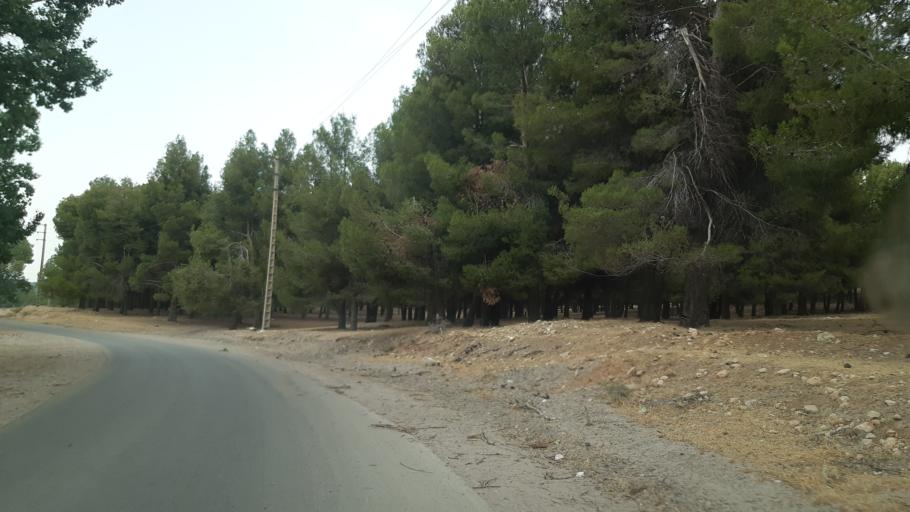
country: MA
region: Meknes-Tafilalet
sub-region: Ifrane
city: Ifrane
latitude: 33.6530
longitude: -5.0262
